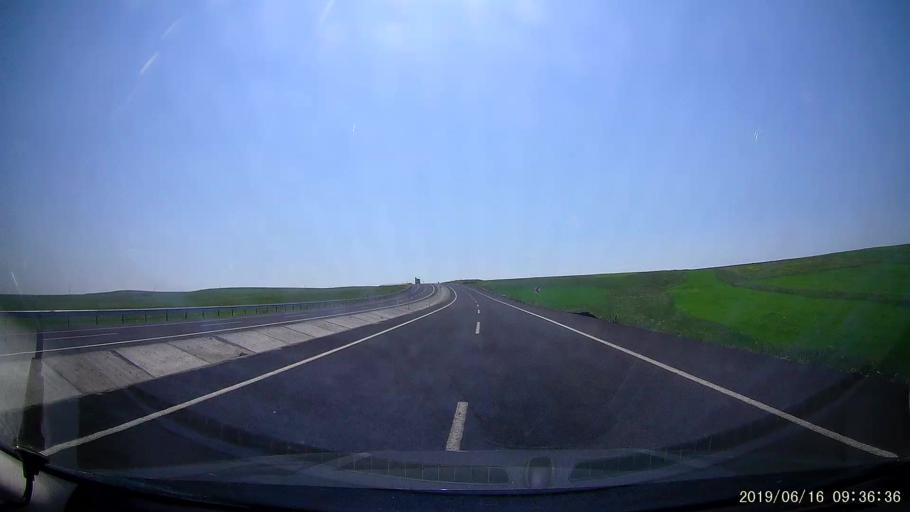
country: TR
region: Kars
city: Kars
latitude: 40.5568
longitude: 43.1758
